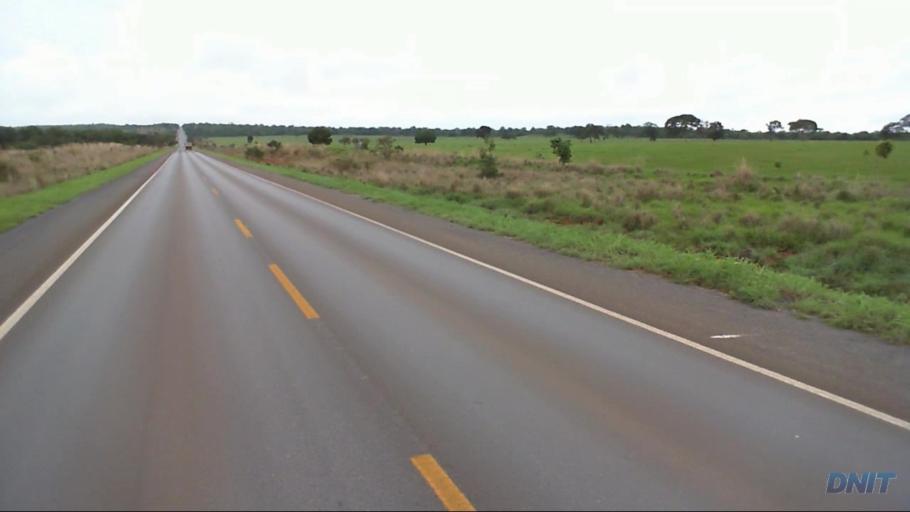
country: BR
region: Goias
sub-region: Padre Bernardo
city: Padre Bernardo
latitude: -15.1739
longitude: -48.3957
